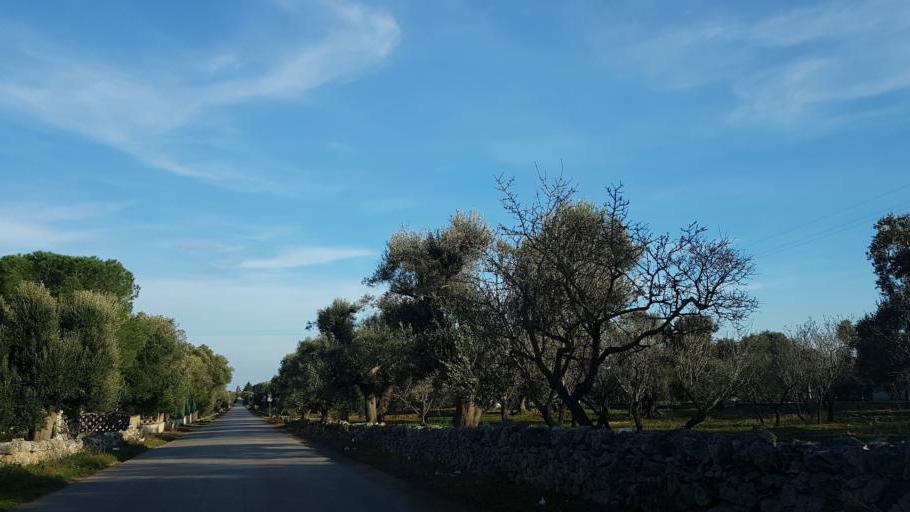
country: IT
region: Apulia
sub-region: Provincia di Brindisi
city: Carovigno
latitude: 40.7057
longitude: 17.7063
